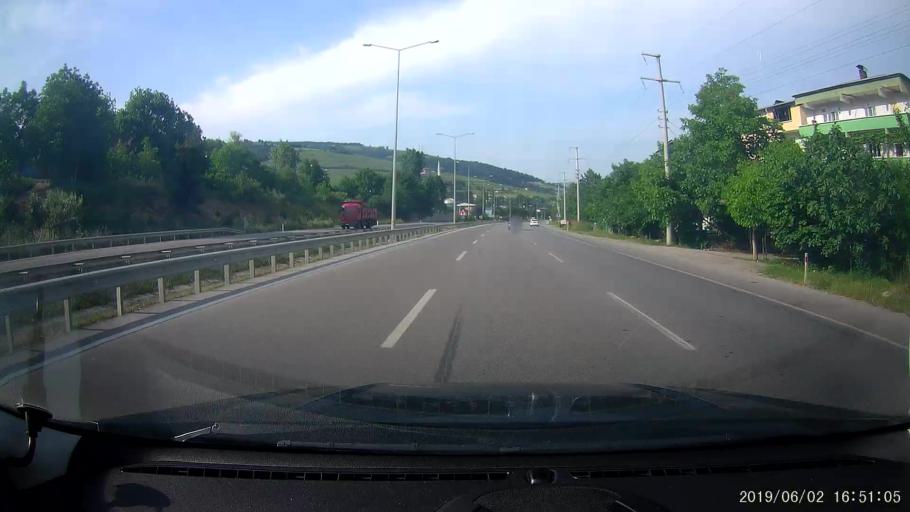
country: TR
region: Samsun
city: Taflan
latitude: 41.2682
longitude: 36.1779
